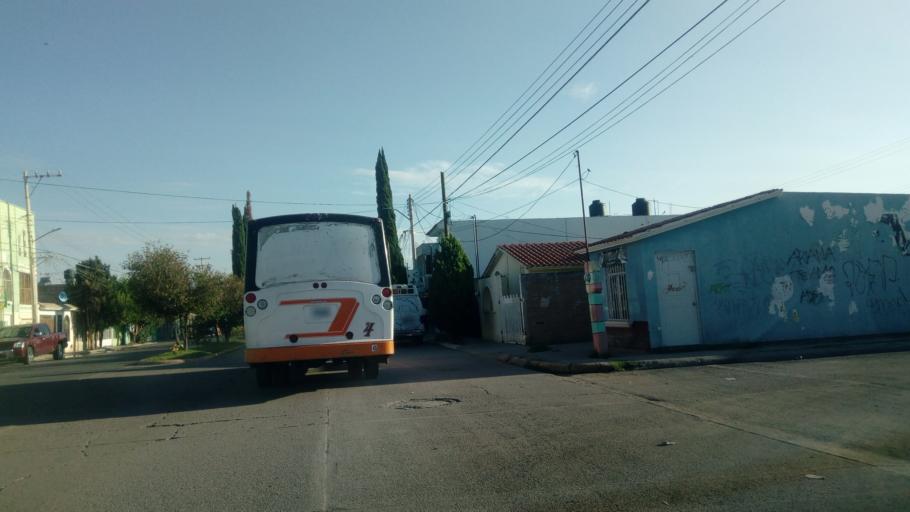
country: MX
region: Durango
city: Victoria de Durango
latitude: 24.0590
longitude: -104.5846
